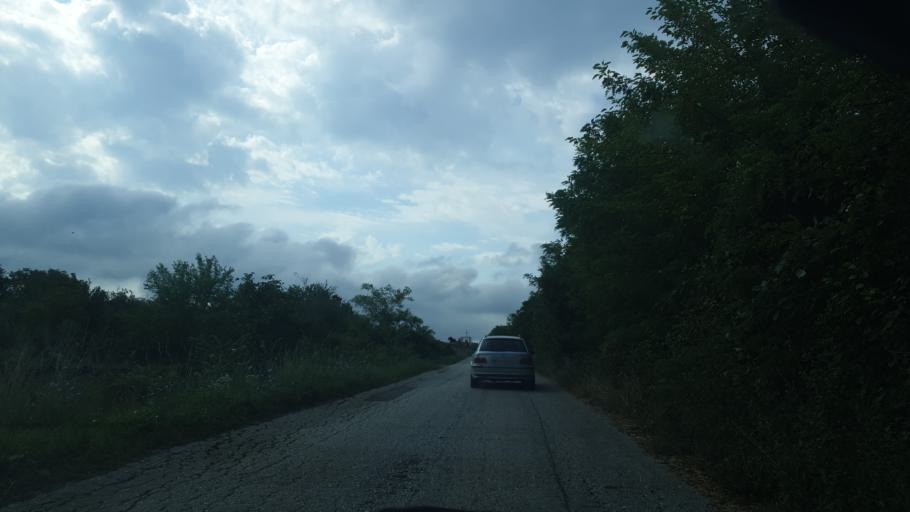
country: RS
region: Central Serbia
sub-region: Sumadijski Okrug
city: Kragujevac
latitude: 44.1009
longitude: 20.7804
